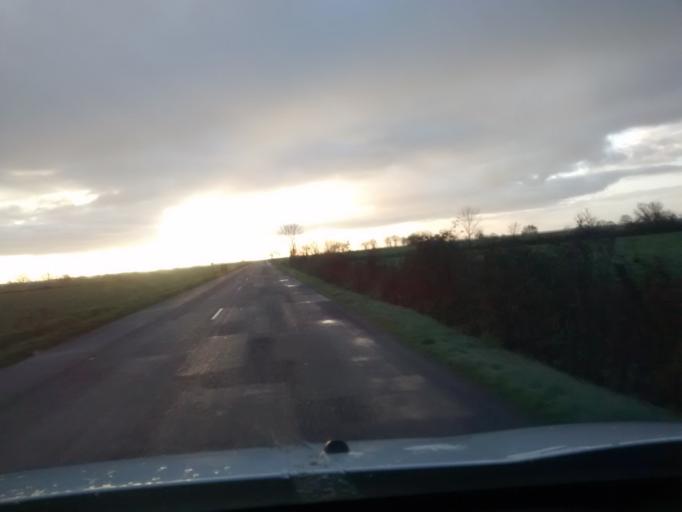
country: FR
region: Brittany
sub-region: Departement d'Ille-et-Vilaine
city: Bais
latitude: 47.9833
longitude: -1.2809
